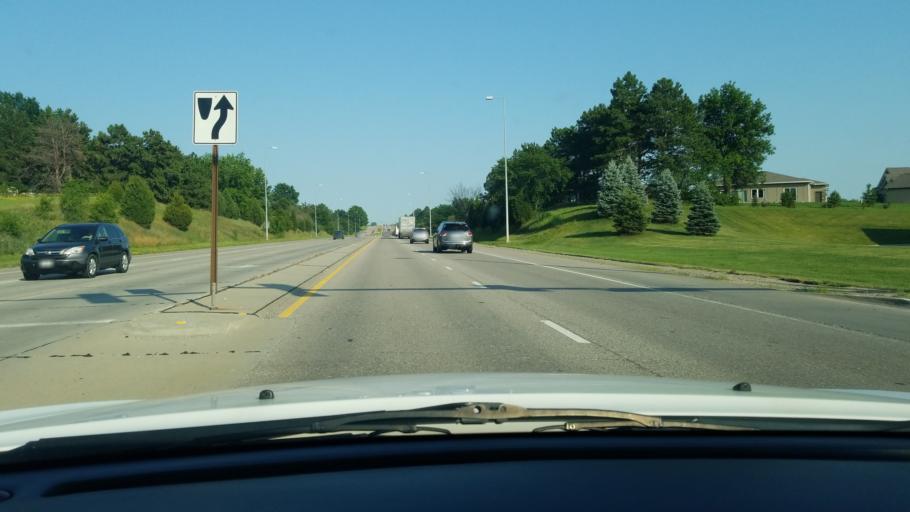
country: US
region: Nebraska
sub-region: Lancaster County
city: Lincoln
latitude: 40.7514
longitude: -96.6350
